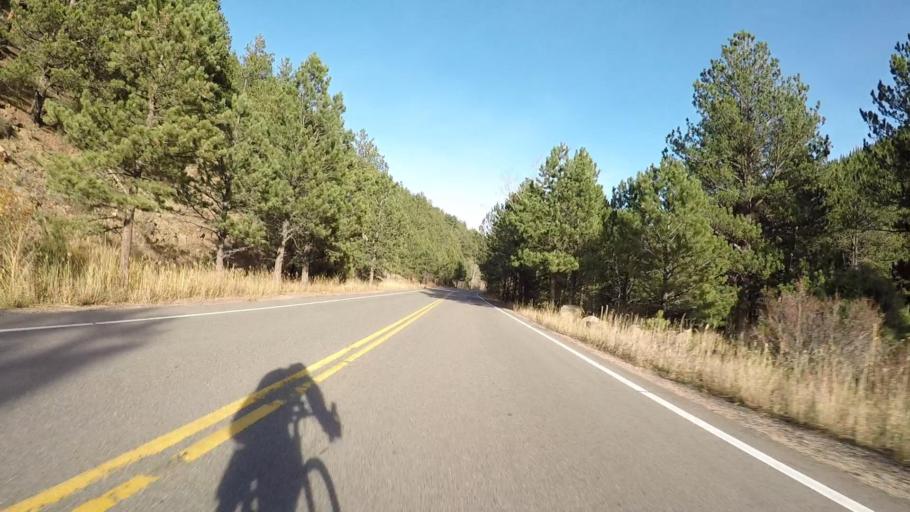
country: US
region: Colorado
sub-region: Boulder County
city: Nederland
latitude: 40.0668
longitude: -105.4528
